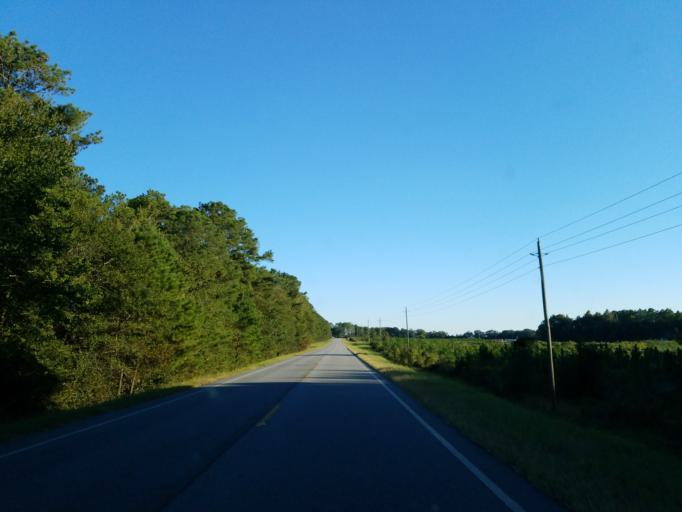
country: US
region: Georgia
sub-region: Worth County
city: Sylvester
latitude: 31.6869
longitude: -83.8813
